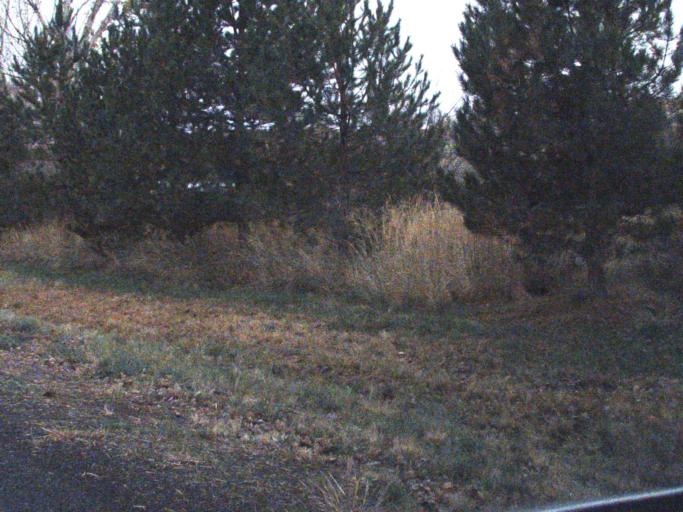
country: US
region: Washington
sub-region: Walla Walla County
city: Waitsburg
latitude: 46.5239
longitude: -118.1326
